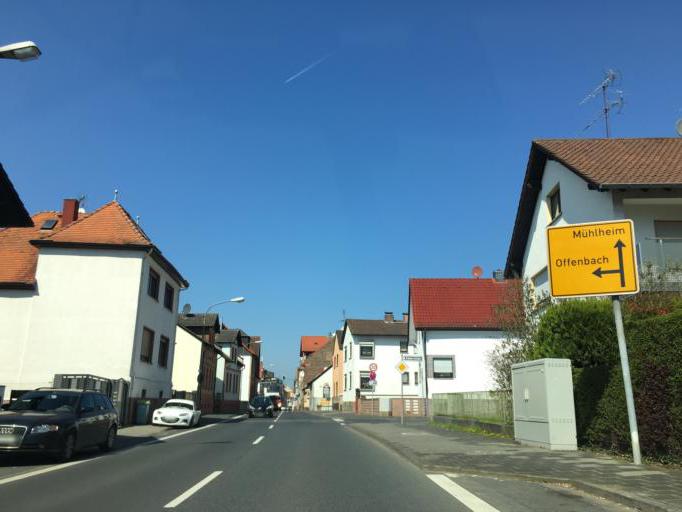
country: DE
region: Hesse
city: Obertshausen
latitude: 50.0948
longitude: 8.8588
